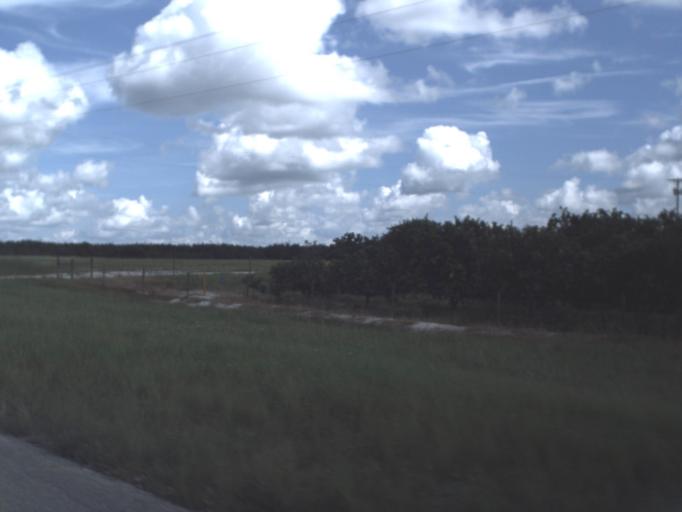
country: US
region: Florida
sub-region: Highlands County
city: Placid Lakes
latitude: 27.1417
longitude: -81.3286
